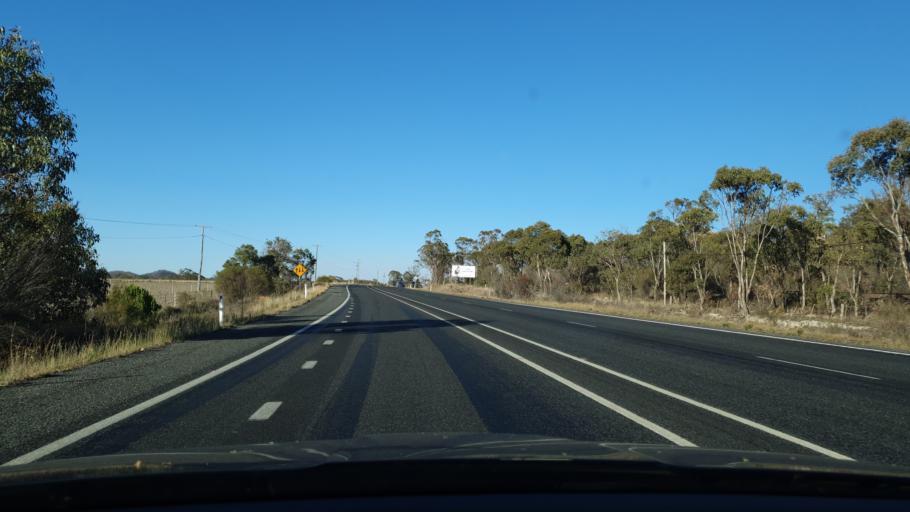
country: AU
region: Queensland
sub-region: Southern Downs
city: Stanthorpe
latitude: -28.6881
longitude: 151.9112
